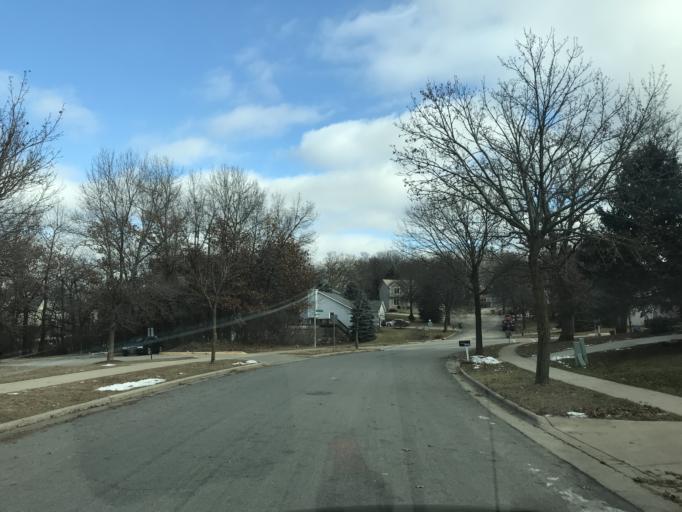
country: US
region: Wisconsin
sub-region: Dane County
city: Monona
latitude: 43.1189
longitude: -89.2986
